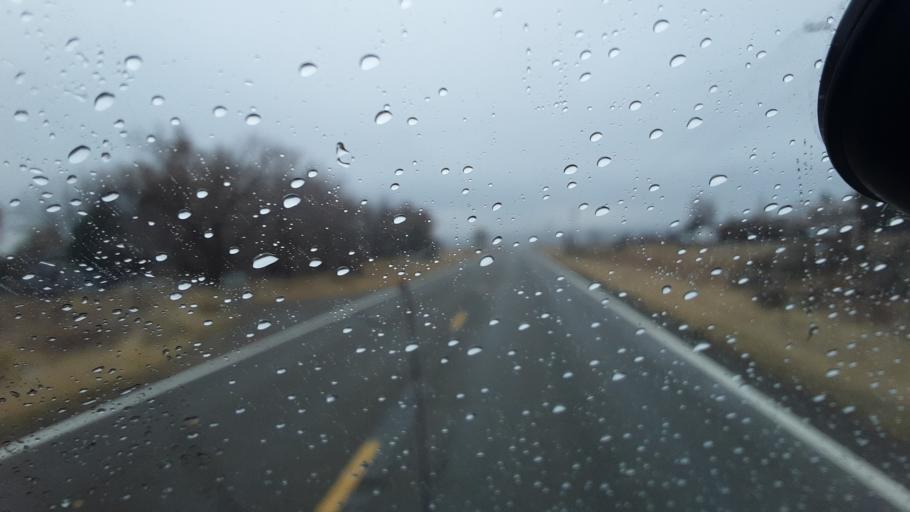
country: US
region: Colorado
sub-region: Montezuma County
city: Mancos
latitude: 37.1140
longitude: -108.1522
